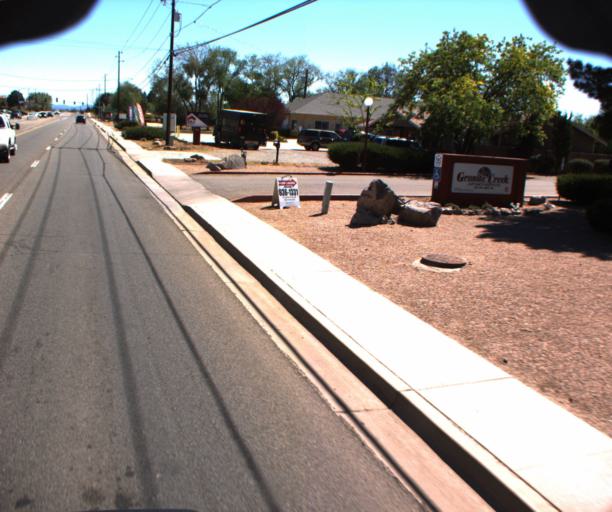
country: US
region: Arizona
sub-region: Yavapai County
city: Chino Valley
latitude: 34.7480
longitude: -112.4545
